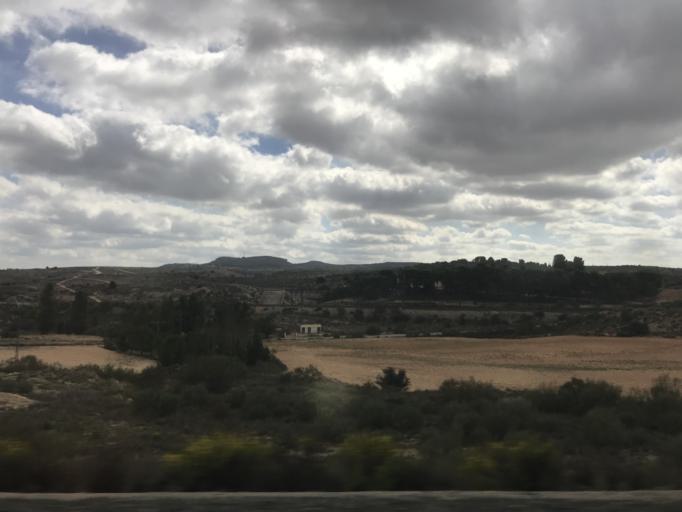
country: ES
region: Castille-La Mancha
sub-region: Provincia de Albacete
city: Almansa
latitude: 38.8785
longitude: -1.1583
